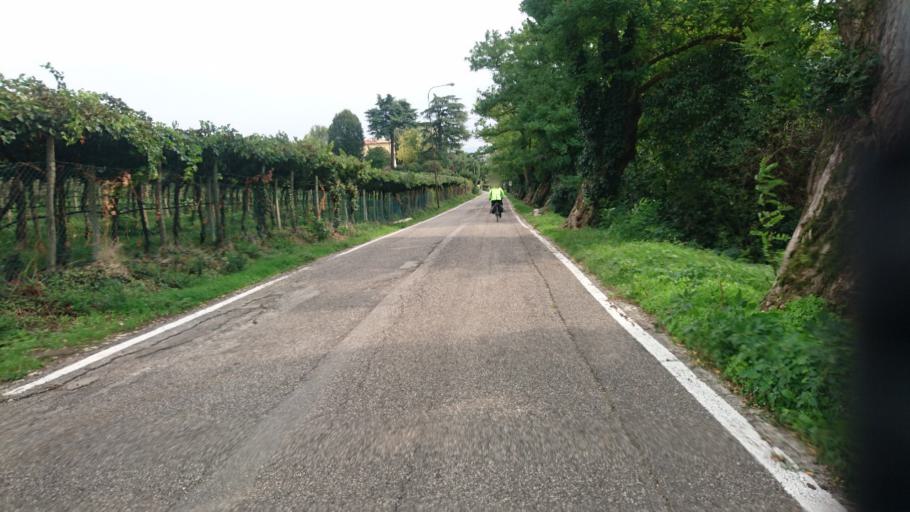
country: IT
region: Veneto
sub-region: Provincia di Verona
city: Caldiero
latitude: 45.4103
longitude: 11.1904
